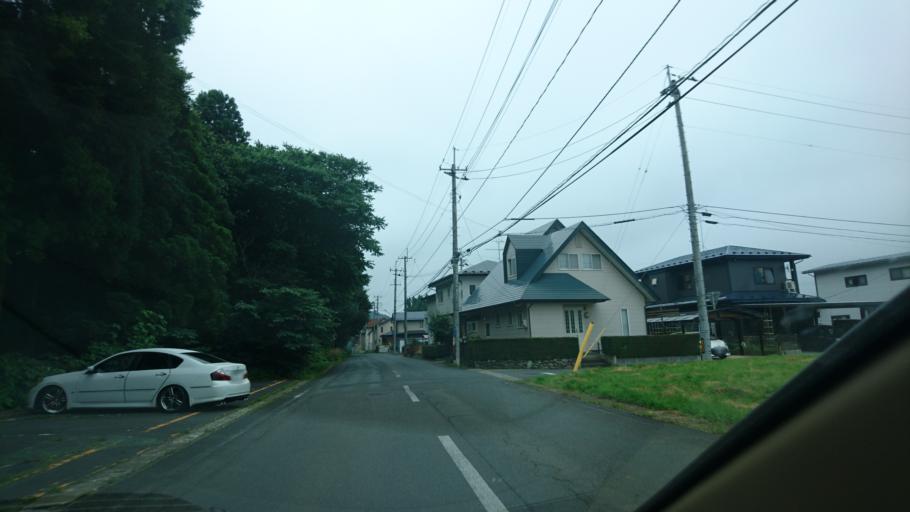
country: JP
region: Iwate
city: Kitakami
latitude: 39.2654
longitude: 141.1091
